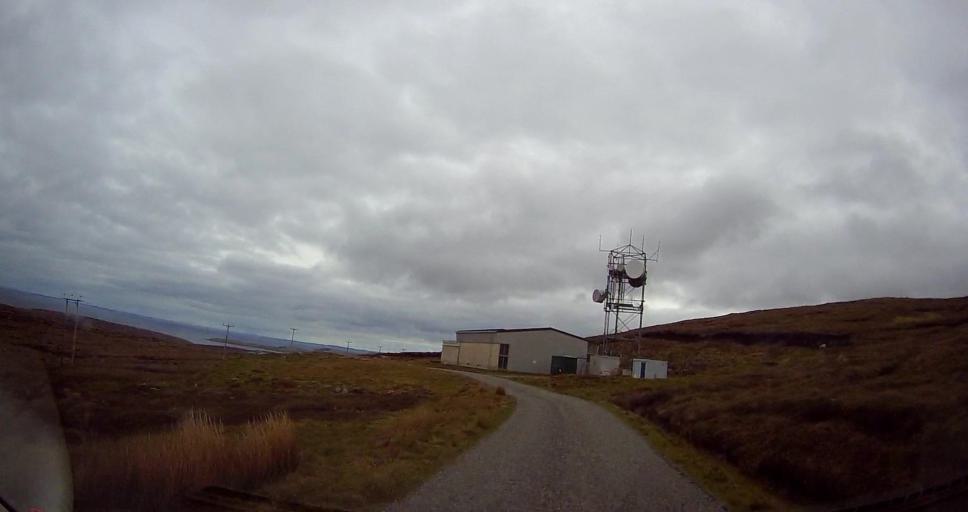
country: GB
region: Scotland
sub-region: Shetland Islands
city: Shetland
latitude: 60.5748
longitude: -1.0678
